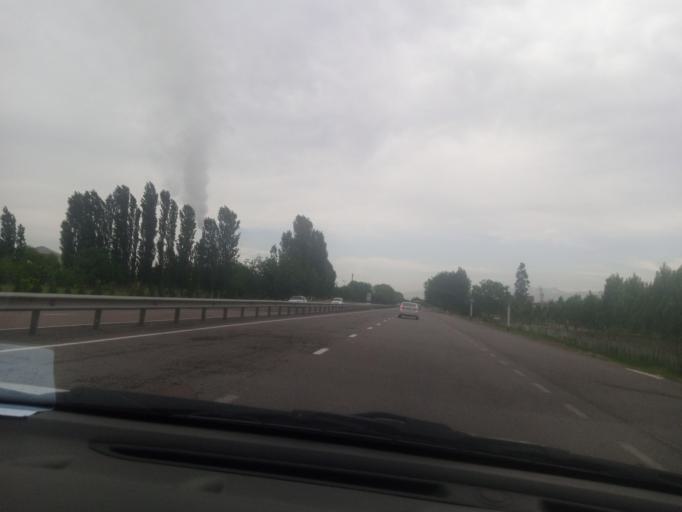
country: UZ
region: Toshkent
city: Ohangaron
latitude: 40.9089
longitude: 69.7836
